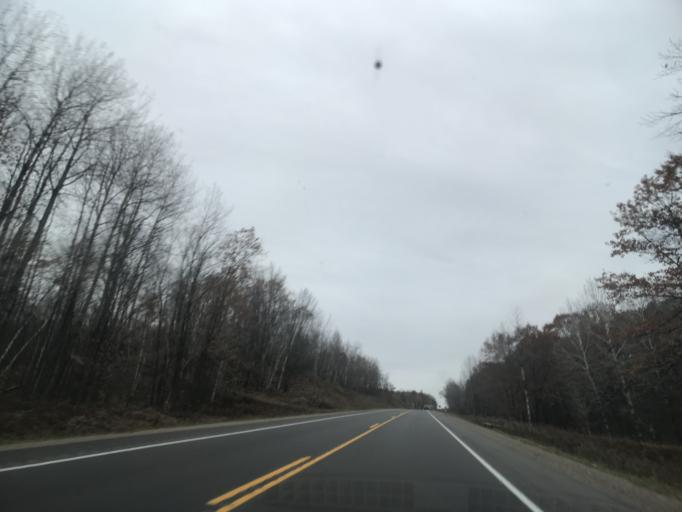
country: US
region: Wisconsin
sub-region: Menominee County
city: Legend Lake
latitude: 45.2793
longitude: -88.5100
